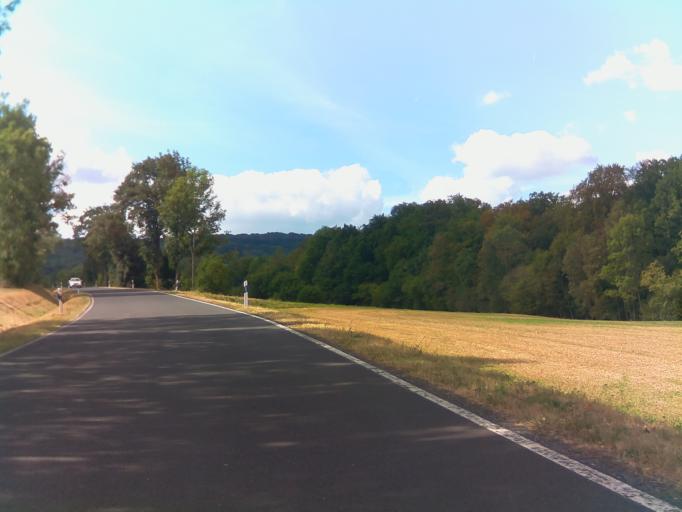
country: DE
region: Bavaria
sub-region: Regierungsbezirk Unterfranken
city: Oberelsbach
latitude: 50.4640
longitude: 10.1152
